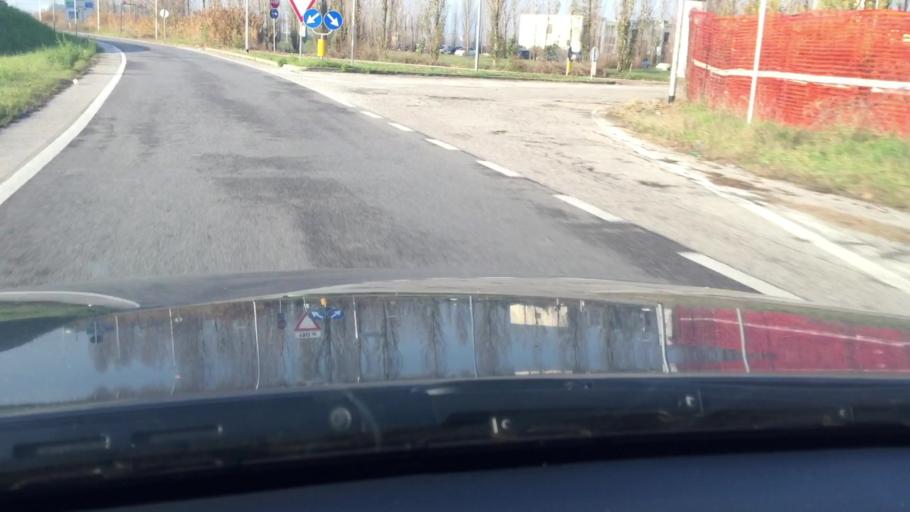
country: IT
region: Emilia-Romagna
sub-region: Provincia di Ferrara
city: Ferrara
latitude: 44.8239
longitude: 11.5921
